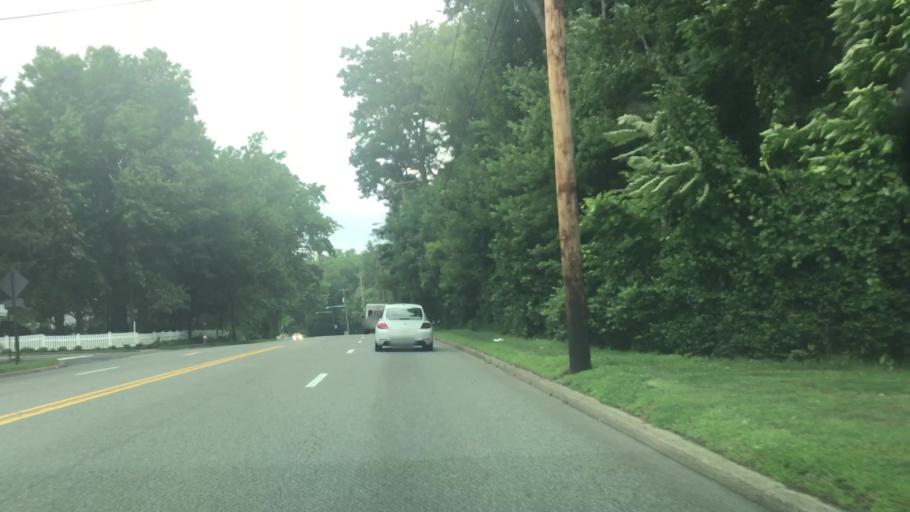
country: US
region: New Jersey
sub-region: Bergen County
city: River Edge
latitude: 40.9242
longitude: -74.0517
